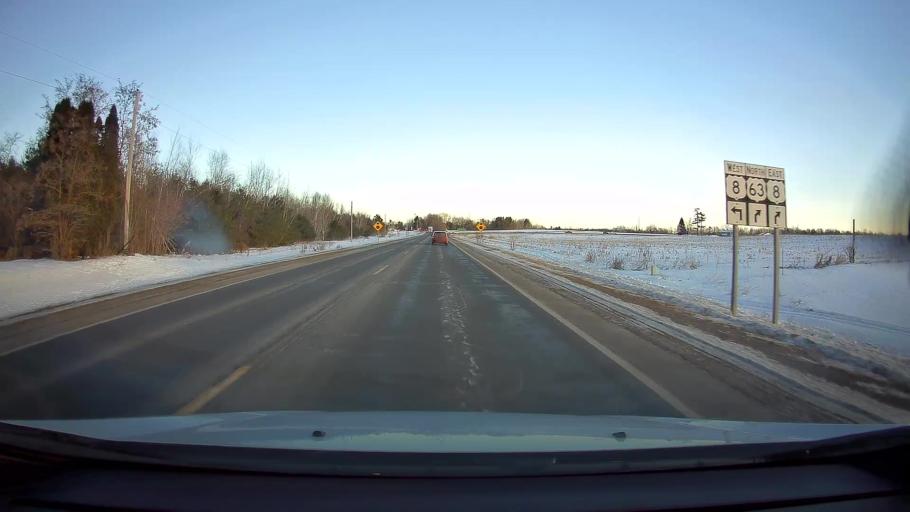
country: US
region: Wisconsin
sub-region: Barron County
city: Turtle Lake
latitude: 45.3916
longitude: -92.1665
